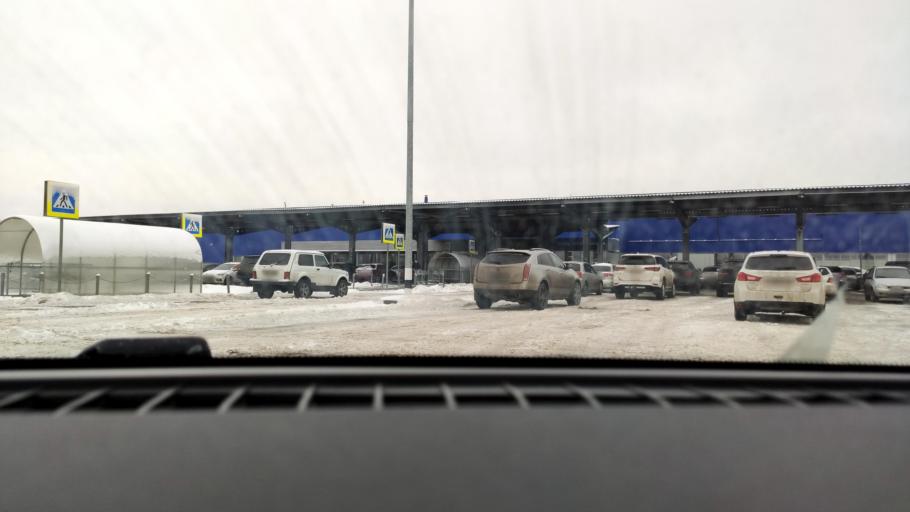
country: RU
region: Samara
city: Samara
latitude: 53.1325
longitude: 50.1386
